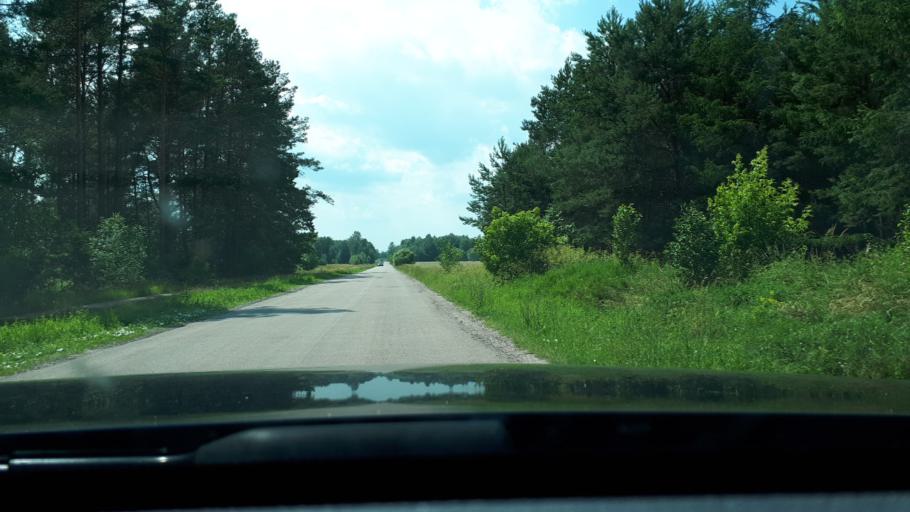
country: PL
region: Podlasie
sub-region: Powiat bialostocki
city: Choroszcz
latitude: 53.1216
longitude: 22.9130
